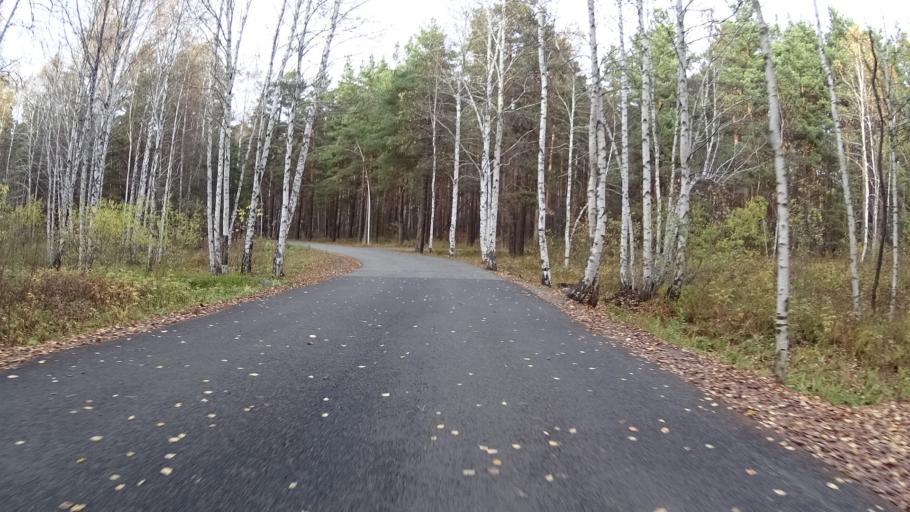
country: RU
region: Chelyabinsk
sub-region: Gorod Chelyabinsk
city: Chelyabinsk
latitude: 55.1387
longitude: 61.3513
